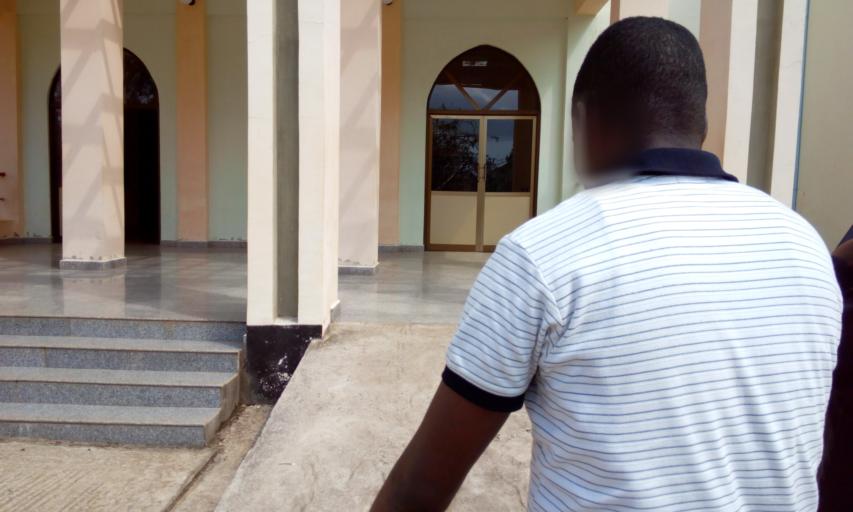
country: TZ
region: Zanzibar Central/South
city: Koani
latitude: -6.1992
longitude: 39.3076
